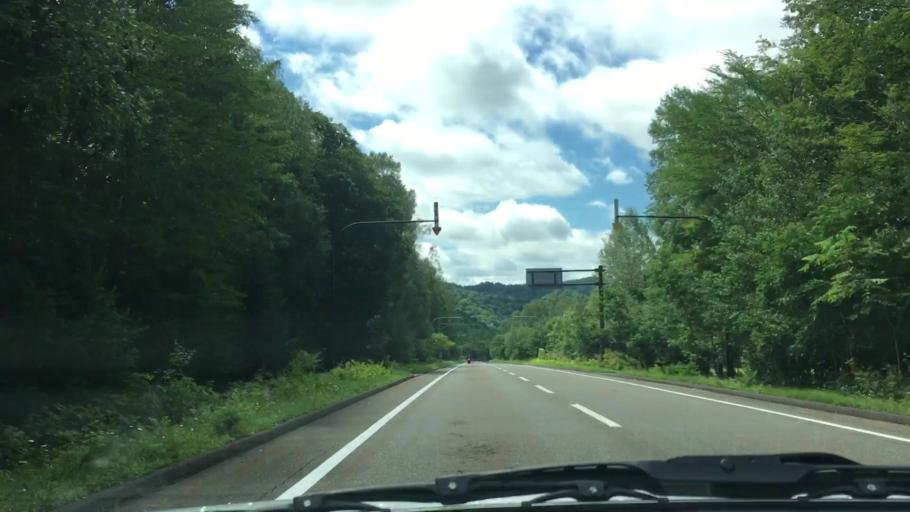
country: JP
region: Hokkaido
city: Kitami
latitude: 43.3962
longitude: 143.9246
